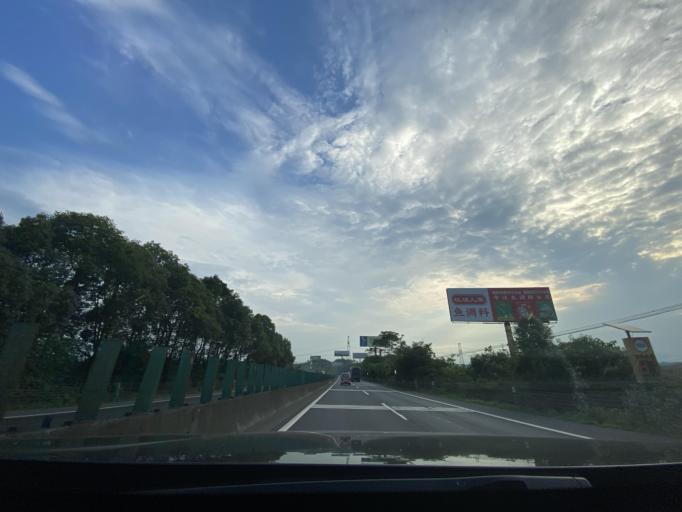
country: CN
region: Sichuan
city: Luojiang
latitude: 31.4037
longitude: 104.5701
